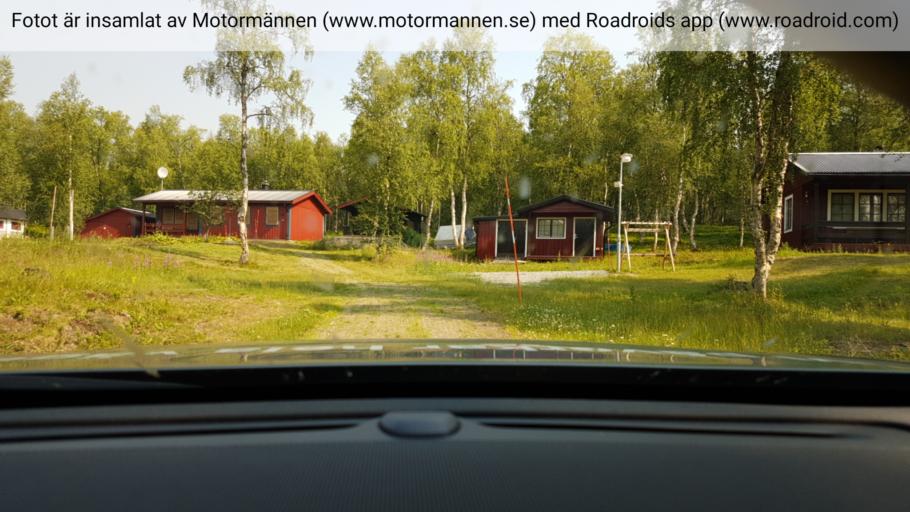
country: NO
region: Nordland
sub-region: Rana
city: Mo i Rana
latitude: 65.7783
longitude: 15.1309
